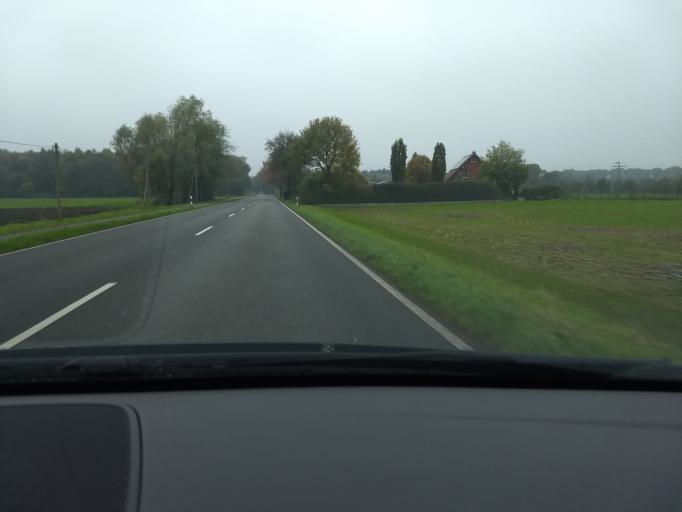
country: DE
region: North Rhine-Westphalia
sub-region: Regierungsbezirk Munster
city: Sudlohn
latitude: 51.9559
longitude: 6.8481
